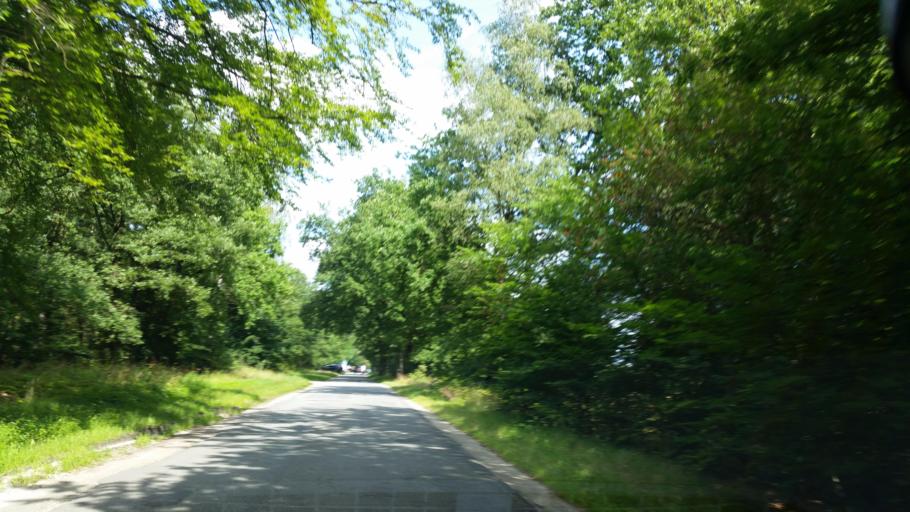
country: DE
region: Lower Saxony
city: Bispingen
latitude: 53.1113
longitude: 9.9109
